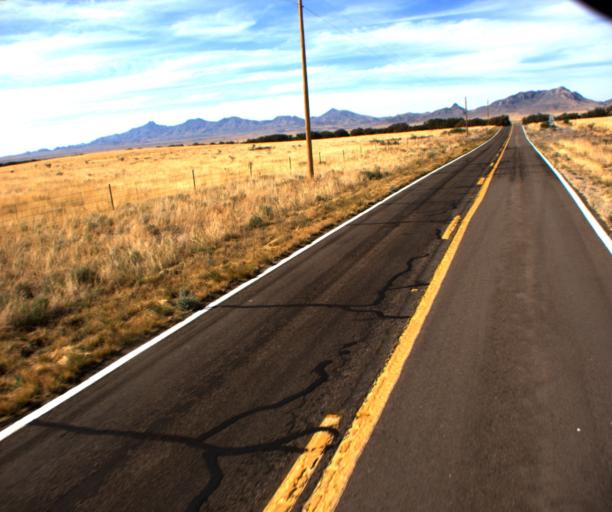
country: US
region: Arizona
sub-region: Cochise County
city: Willcox
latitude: 31.9975
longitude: -109.4400
